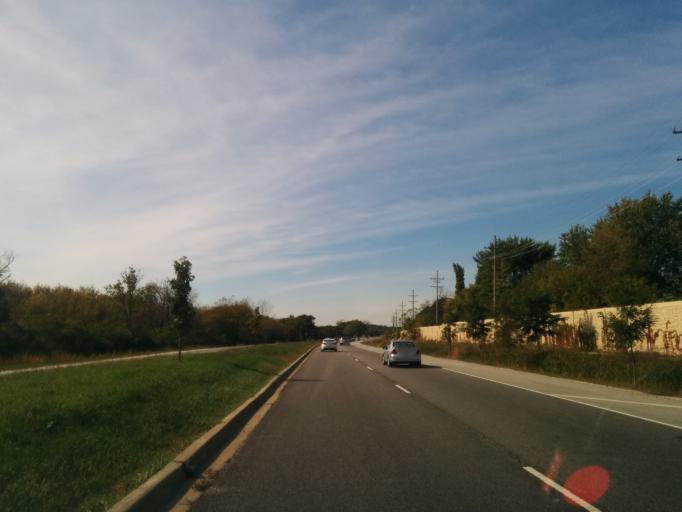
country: US
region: Illinois
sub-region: DuPage County
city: Wheaton
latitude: 41.8288
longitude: -88.1200
